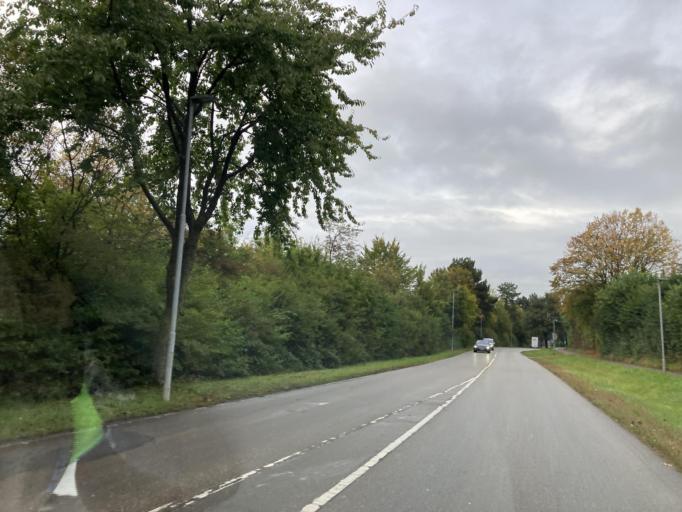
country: DE
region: Baden-Wuerttemberg
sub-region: Freiburg Region
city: Mullheim
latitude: 47.7991
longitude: 7.6244
